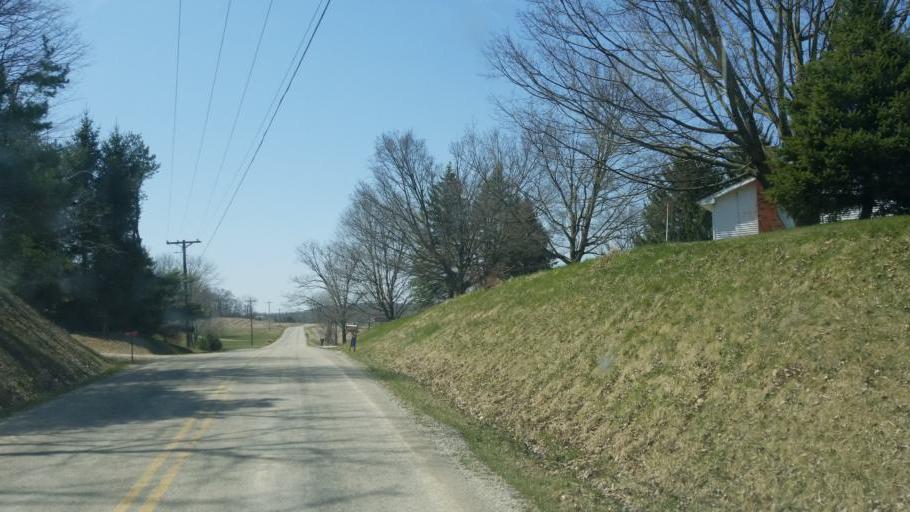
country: US
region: Ohio
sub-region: Ashland County
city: Loudonville
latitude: 40.7530
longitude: -82.2362
